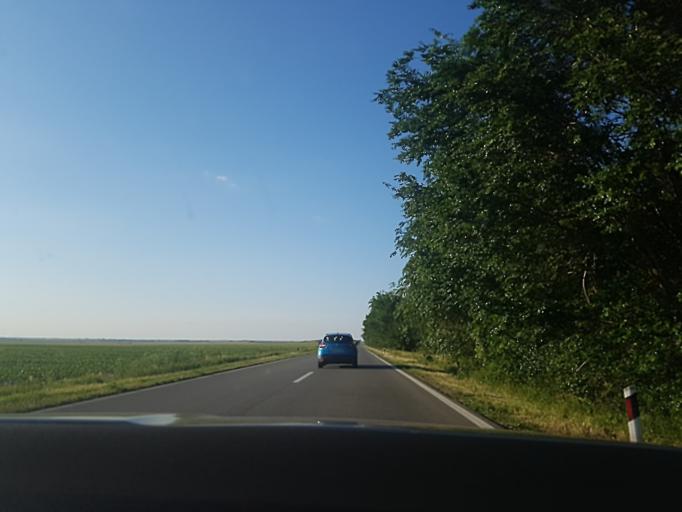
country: RS
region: Autonomna Pokrajina Vojvodina
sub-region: Juznobanatski Okrug
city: Vrsac
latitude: 45.1795
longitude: 21.2955
